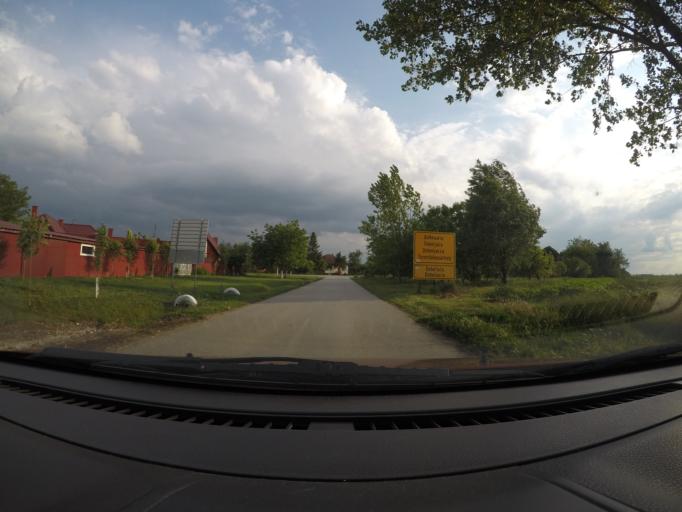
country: RS
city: Debeljaca
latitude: 45.0792
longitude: 20.6003
